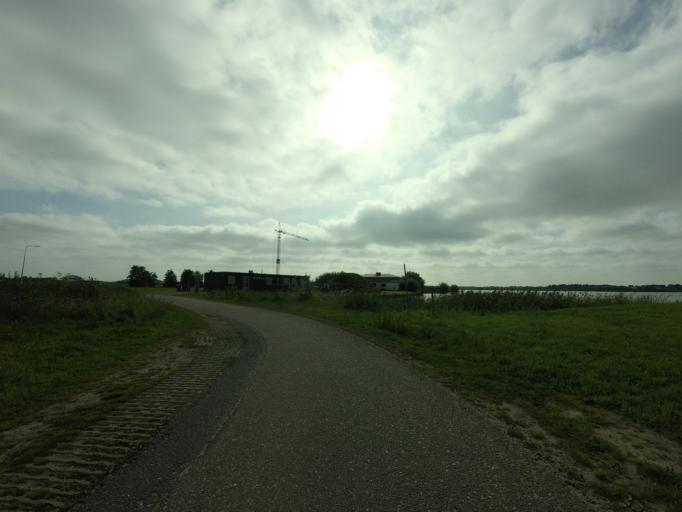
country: NL
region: Overijssel
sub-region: Gemeente Steenwijkerland
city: Steenwijk
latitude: 52.8062
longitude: 6.1404
